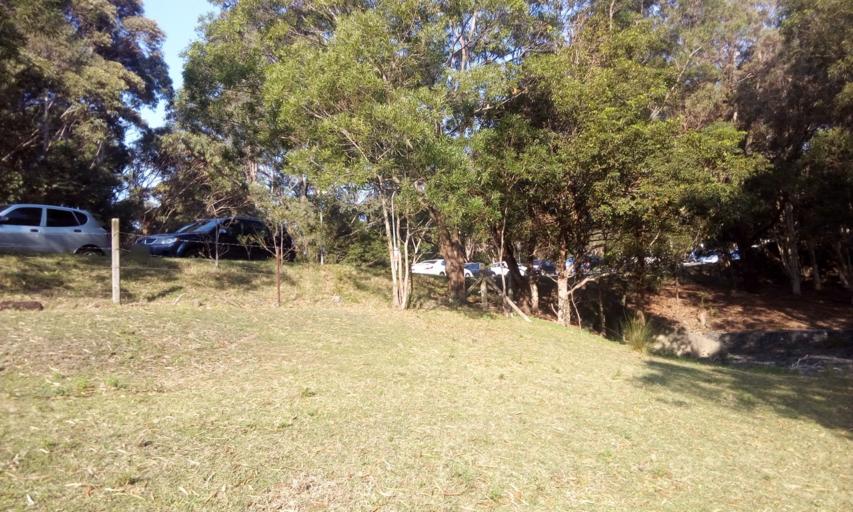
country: AU
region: New South Wales
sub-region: Wollongong
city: Mount Ousley
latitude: -34.4043
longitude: 150.8725
